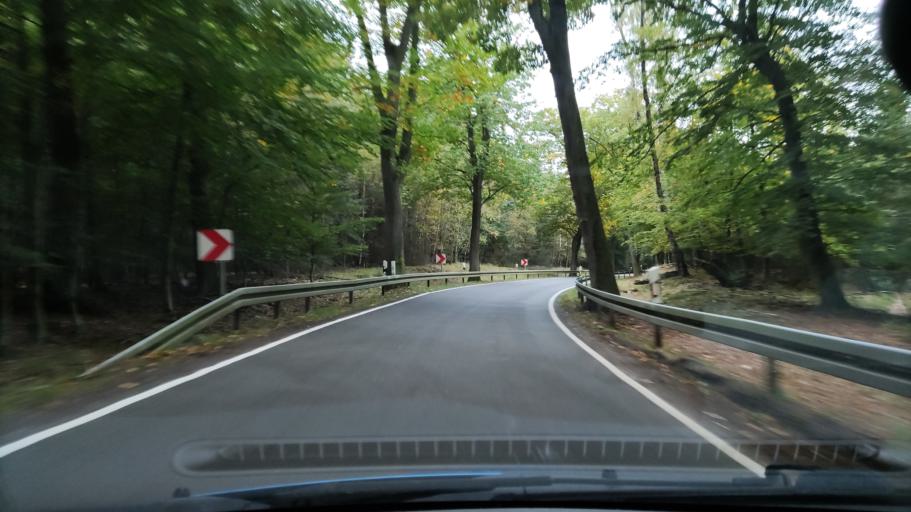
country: DE
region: Mecklenburg-Vorpommern
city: Zarrentin
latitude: 53.4519
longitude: 10.9346
